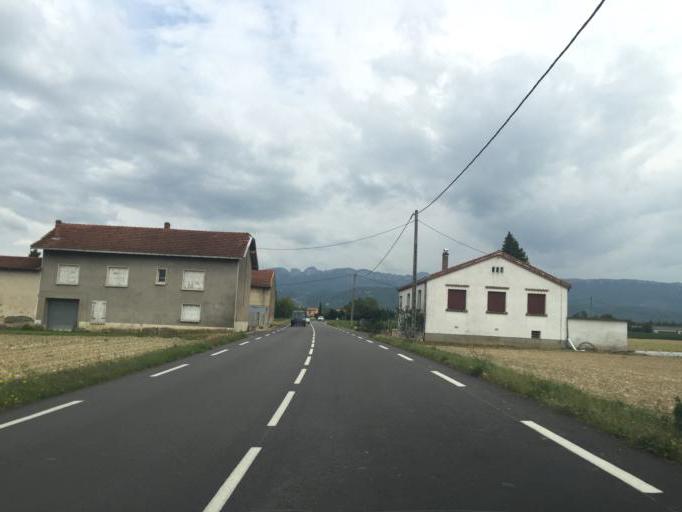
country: FR
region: Rhone-Alpes
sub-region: Departement de la Drome
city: Chatuzange-le-Goubet
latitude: 44.9668
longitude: 5.0669
